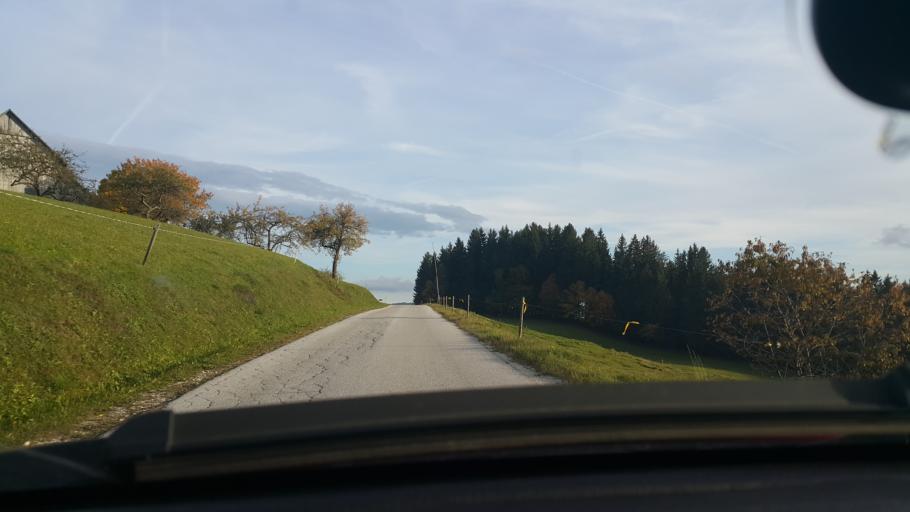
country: SI
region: Mislinja
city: Mislinja
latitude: 46.4255
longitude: 15.2641
